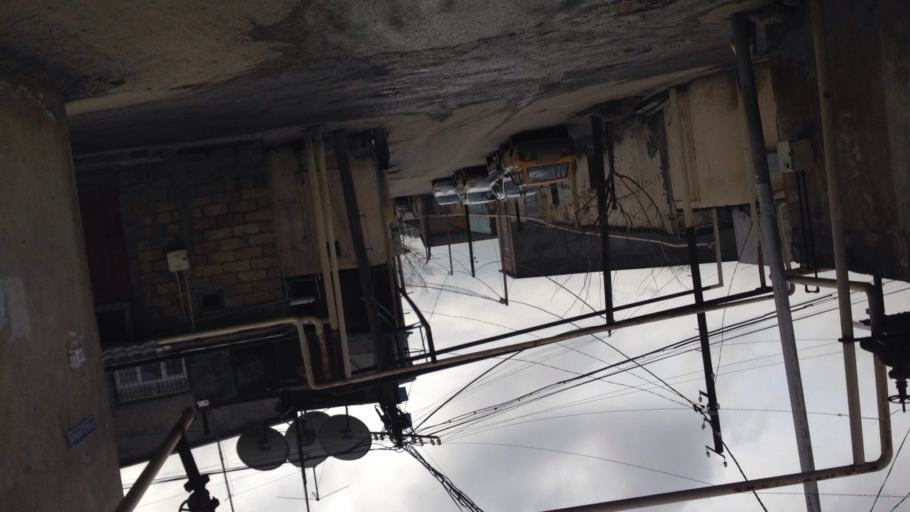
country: AZ
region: Baki
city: Bilajari
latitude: 40.4007
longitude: 49.8277
